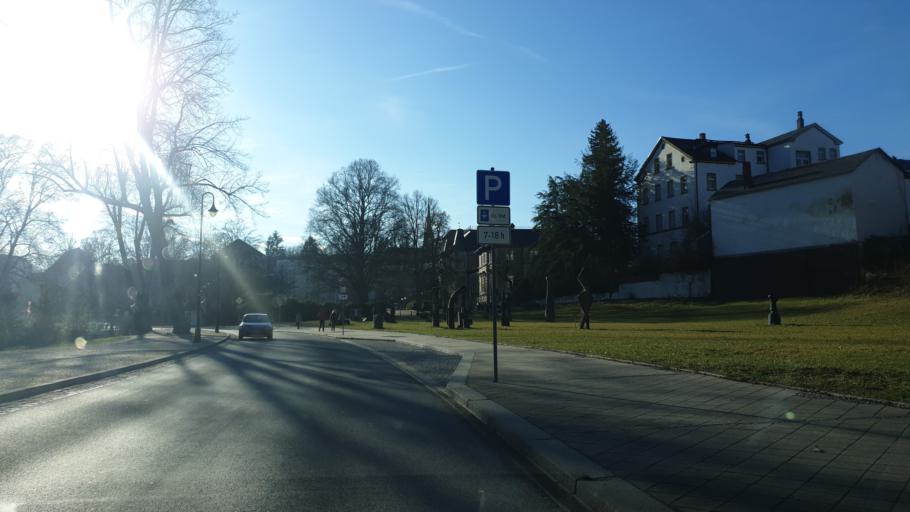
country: DE
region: Saxony
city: Bad Elster
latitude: 50.2848
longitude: 12.2382
